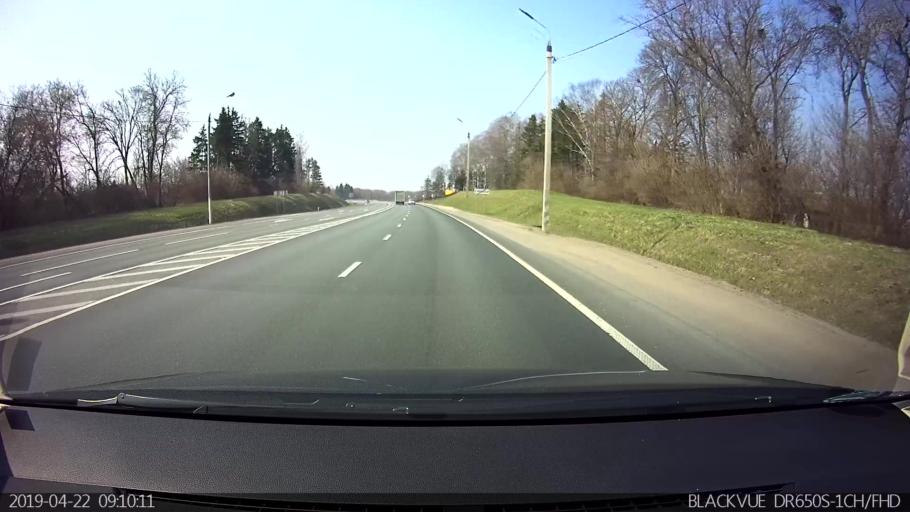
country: RU
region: Smolensk
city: Katyn'
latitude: 54.8432
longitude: 31.6705
